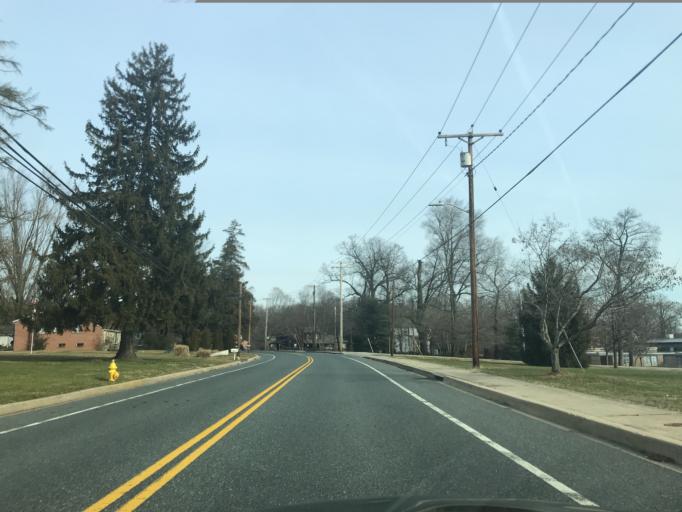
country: US
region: Maryland
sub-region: Harford County
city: Aberdeen
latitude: 39.5172
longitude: -76.1721
